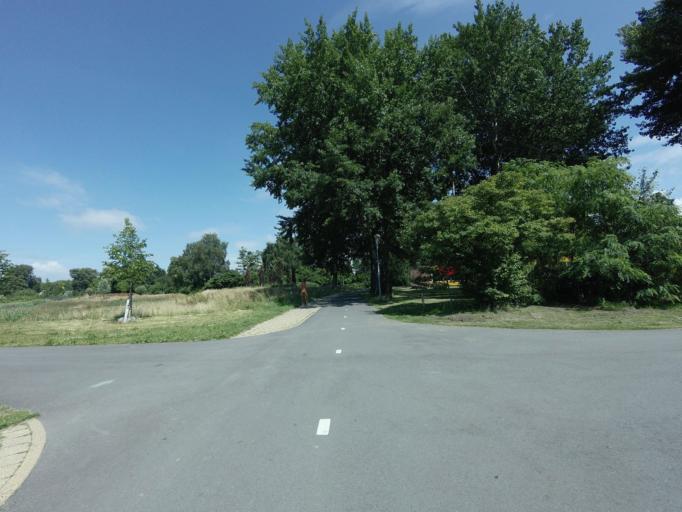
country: NL
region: Flevoland
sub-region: Gemeente Almere
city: Almere Stad
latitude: 52.3407
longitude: 5.2140
